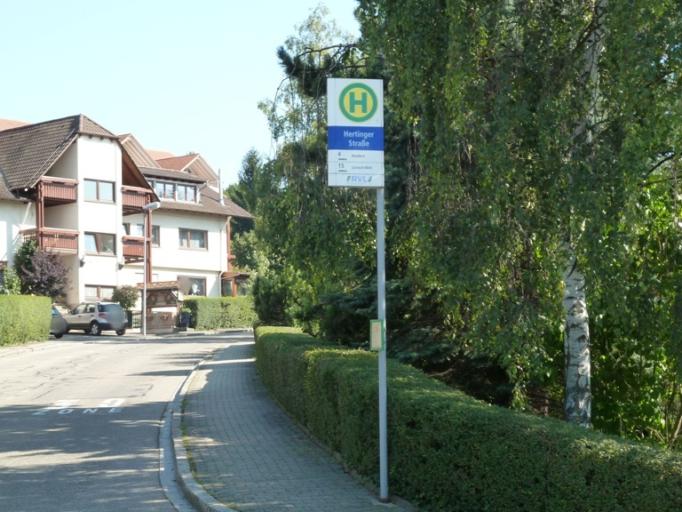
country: DE
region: Baden-Wuerttemberg
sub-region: Freiburg Region
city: Bad Bellingen
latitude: 47.7303
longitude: 7.5578
